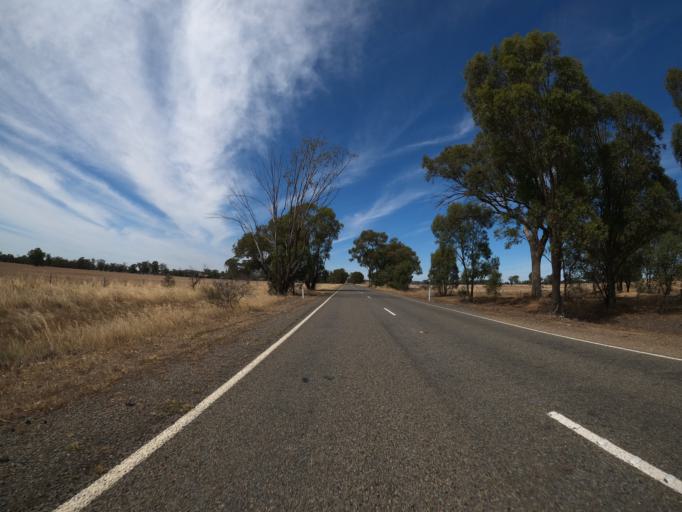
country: AU
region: Victoria
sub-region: Benalla
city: Benalla
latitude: -36.2876
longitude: 145.9523
